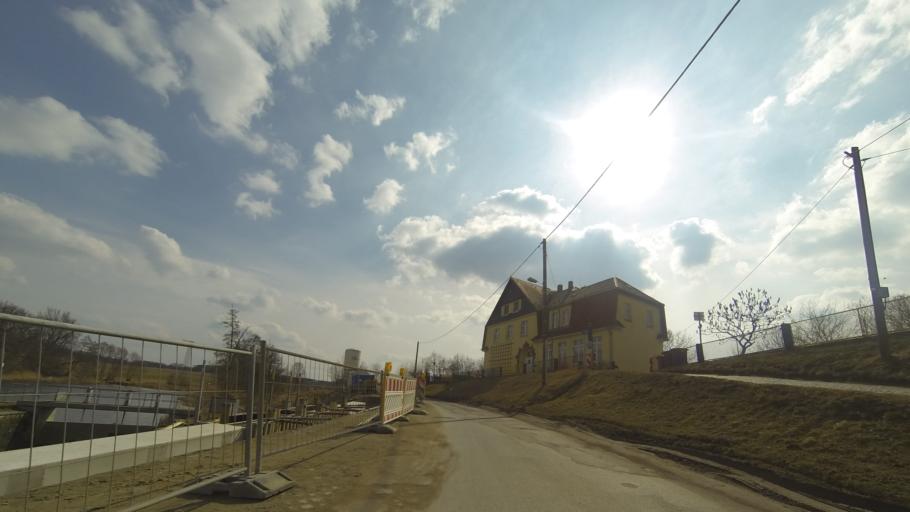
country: DE
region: Saxony
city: Moritzburg
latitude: 51.1449
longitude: 13.7404
